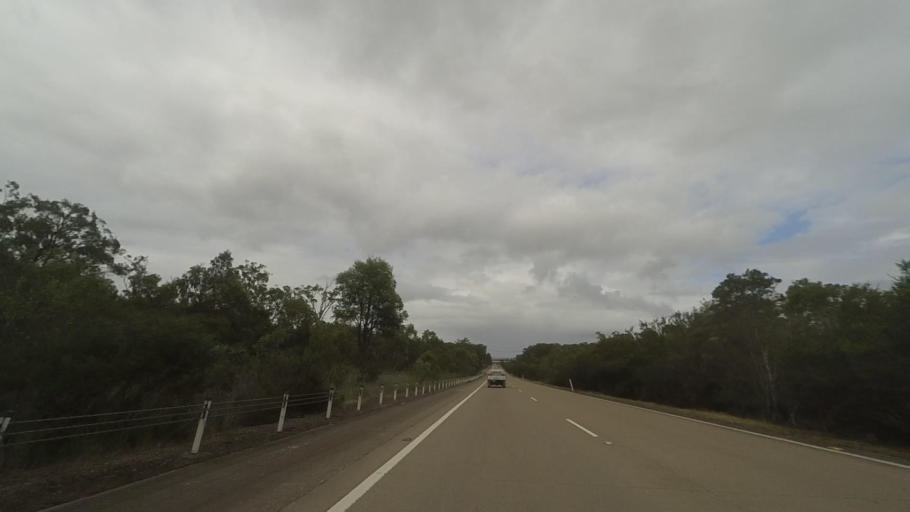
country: AU
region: New South Wales
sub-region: Port Stephens Shire
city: Medowie
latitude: -32.6358
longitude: 151.9351
